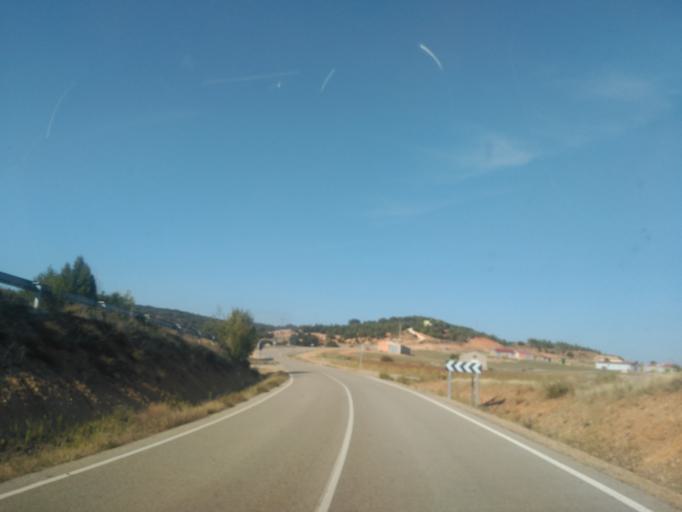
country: ES
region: Castille and Leon
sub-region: Provincia de Soria
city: Alcubilla de Avellaneda
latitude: 41.7247
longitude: -3.3104
